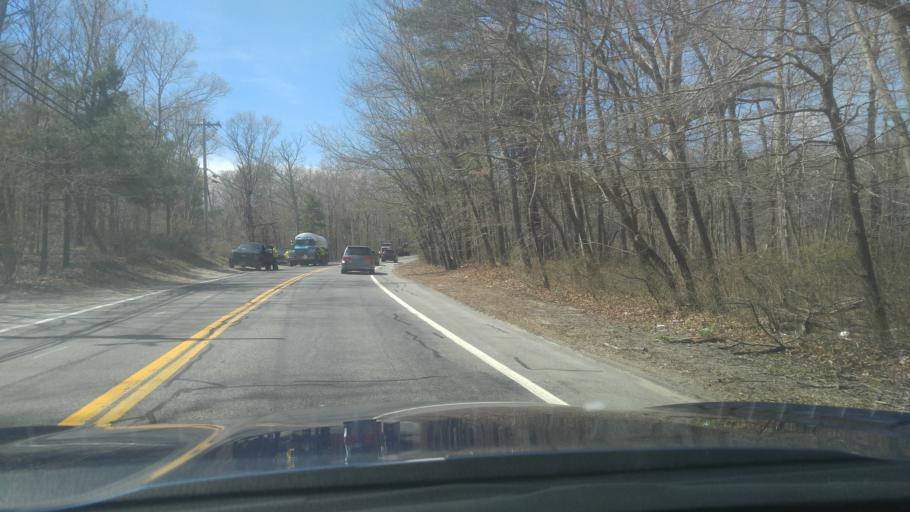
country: US
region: Rhode Island
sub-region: Washington County
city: Exeter
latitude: 41.5791
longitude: -71.6101
